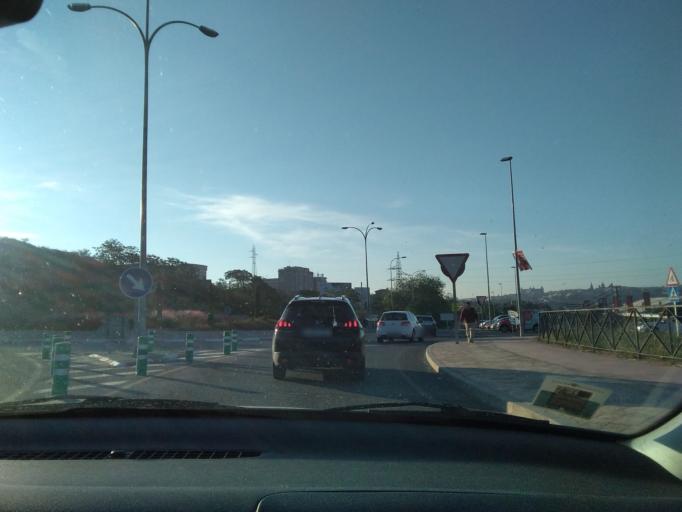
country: ES
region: Castille-La Mancha
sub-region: Province of Toledo
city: Toledo
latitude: 39.8793
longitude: -4.0481
